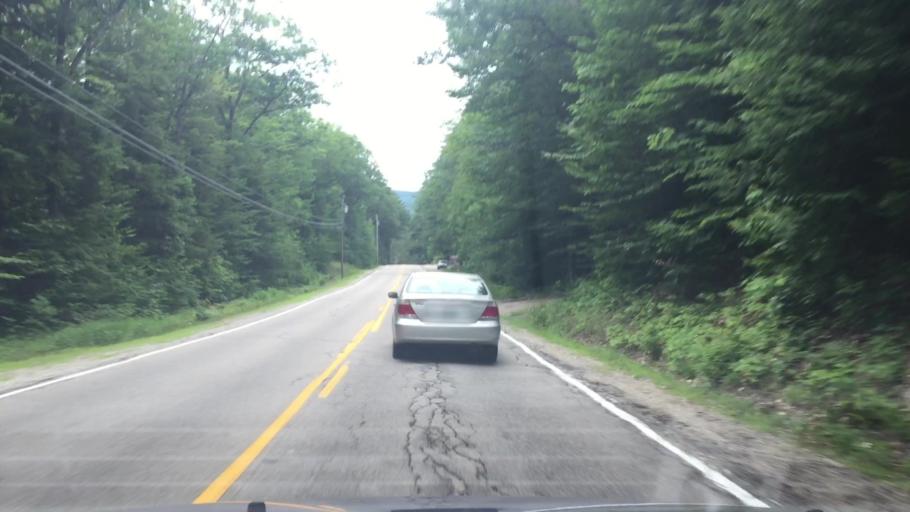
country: US
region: New Hampshire
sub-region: Carroll County
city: Conway
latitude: 43.9307
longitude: -71.0853
